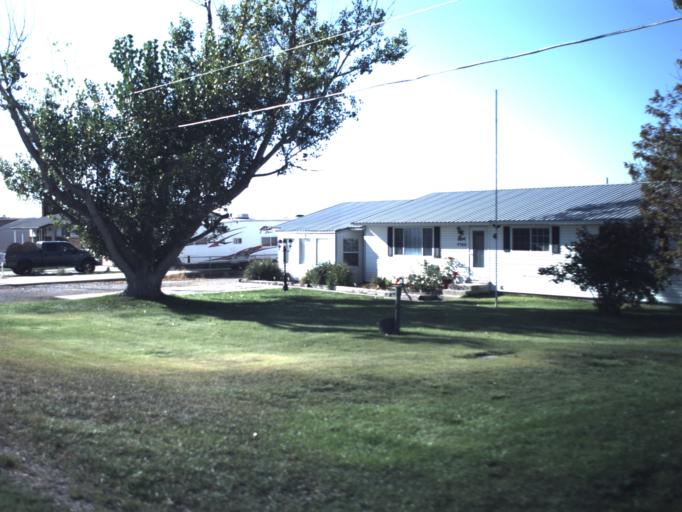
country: US
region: Utah
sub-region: Weber County
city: Hooper
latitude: 41.1399
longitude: -112.1141
